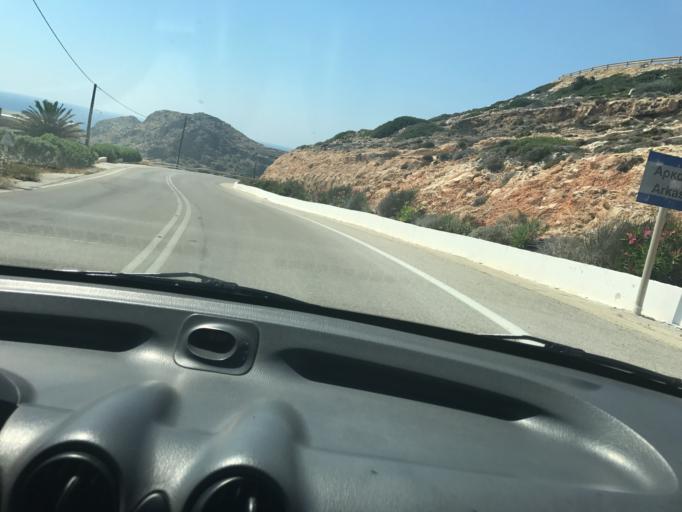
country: GR
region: South Aegean
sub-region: Nomos Dodekanisou
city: Karpathos
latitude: 35.4710
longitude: 27.1193
